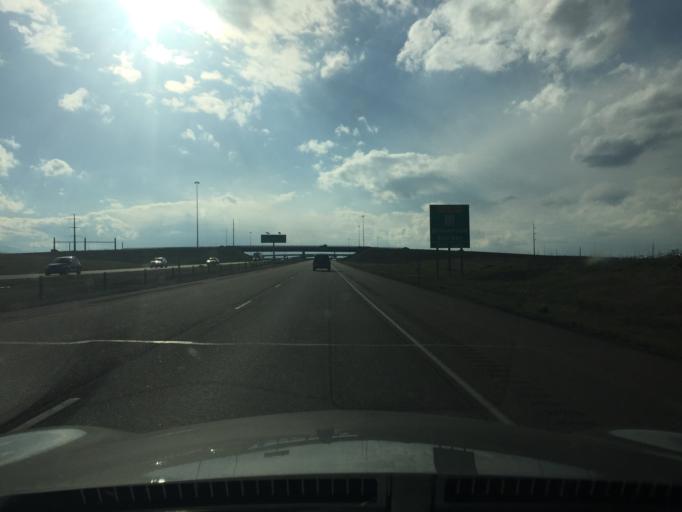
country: US
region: Colorado
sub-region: Adams County
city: Northglenn
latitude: 39.9789
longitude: -104.9737
